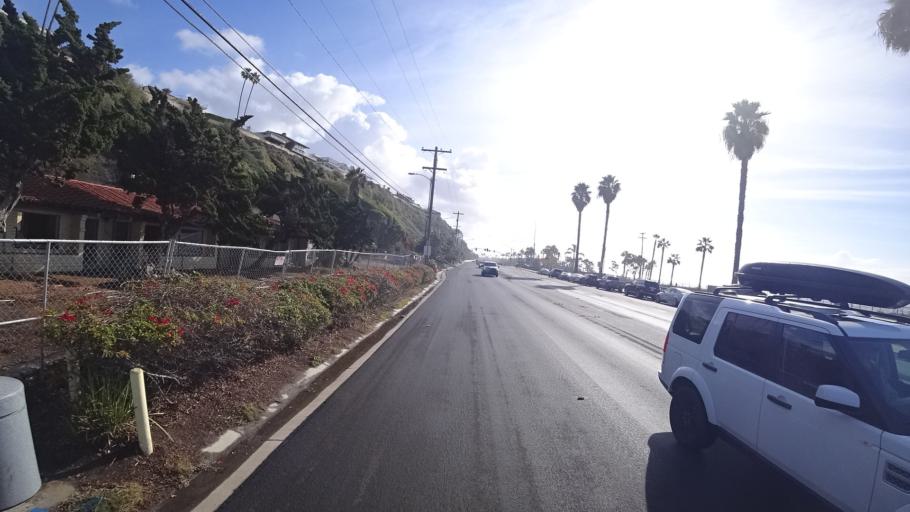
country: US
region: California
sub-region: Orange County
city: Dana Point
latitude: 33.4566
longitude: -117.6693
